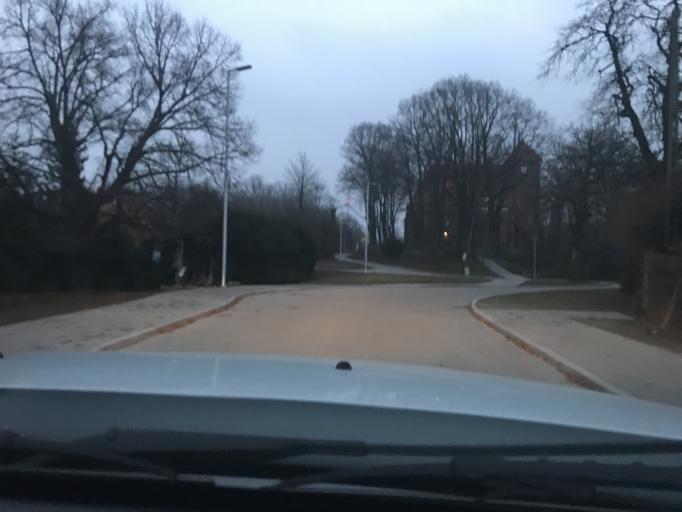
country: PL
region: West Pomeranian Voivodeship
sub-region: Powiat slawienski
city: Darlowo
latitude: 54.4787
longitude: 16.5107
